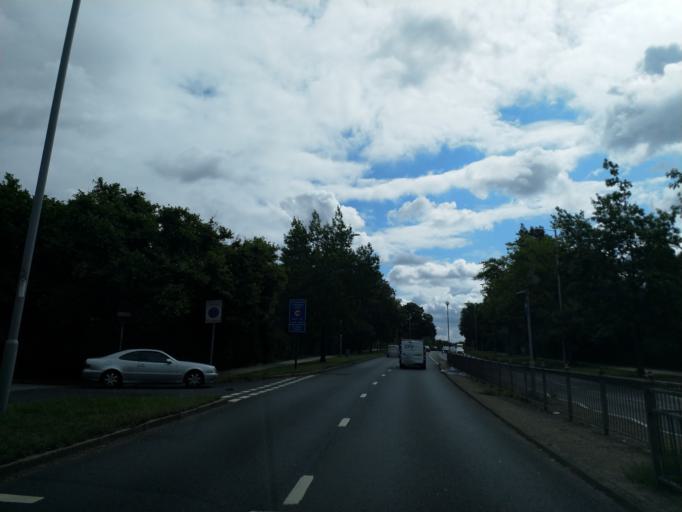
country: GB
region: England
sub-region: Greater London
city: Belsize Park
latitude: 51.5848
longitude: -0.1729
